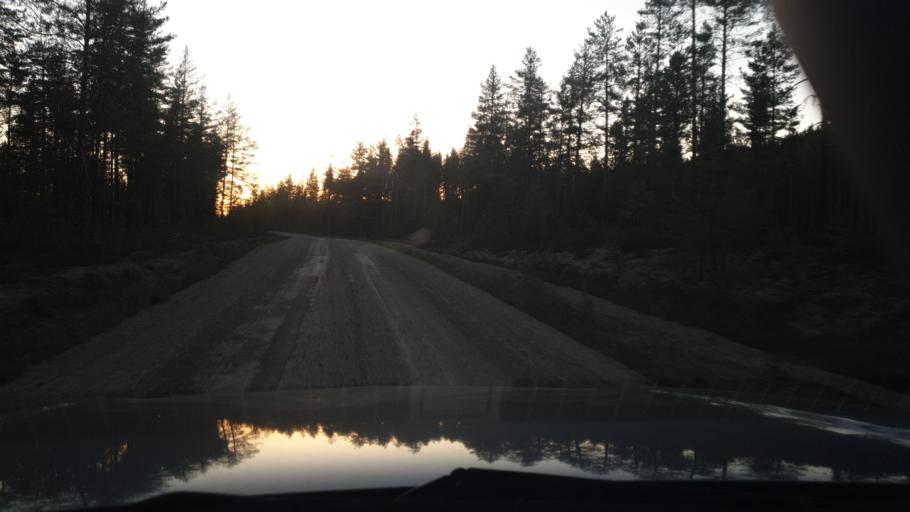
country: SE
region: Vaesternorrland
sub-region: Ange Kommun
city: Ange
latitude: 62.2067
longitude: 15.5478
